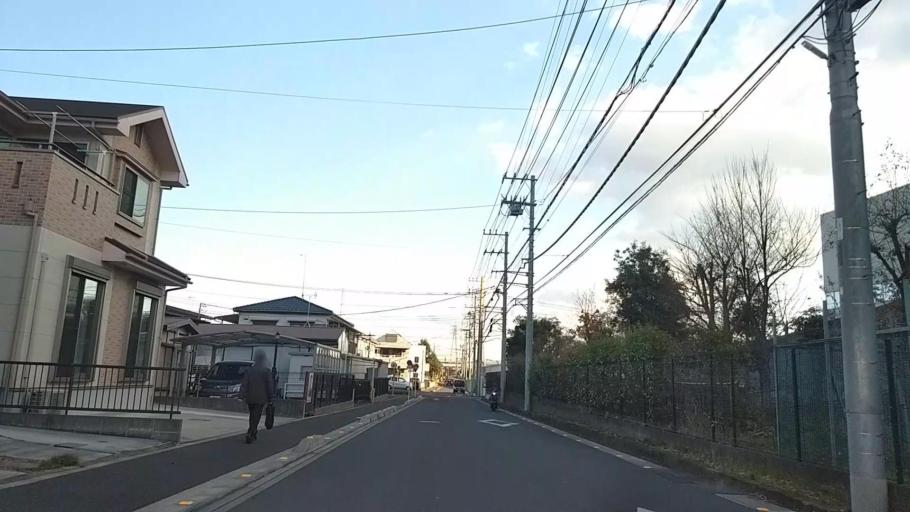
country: JP
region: Kanagawa
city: Atsugi
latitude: 35.4512
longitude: 139.3399
